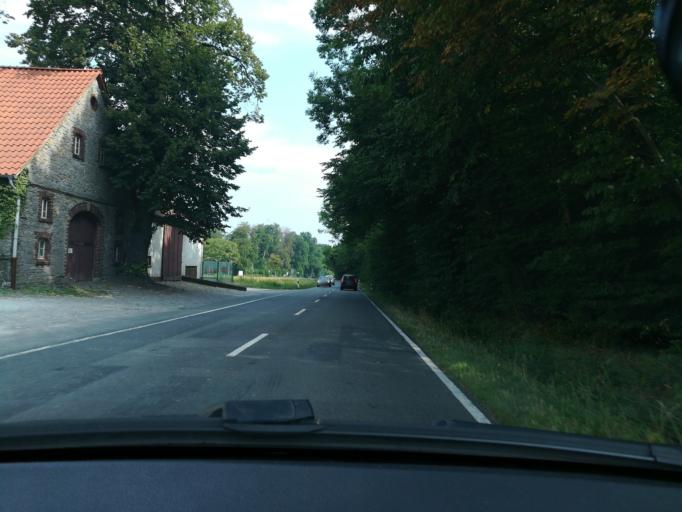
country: DE
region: North Rhine-Westphalia
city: Borgholzhausen
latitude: 52.1236
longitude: 8.3203
